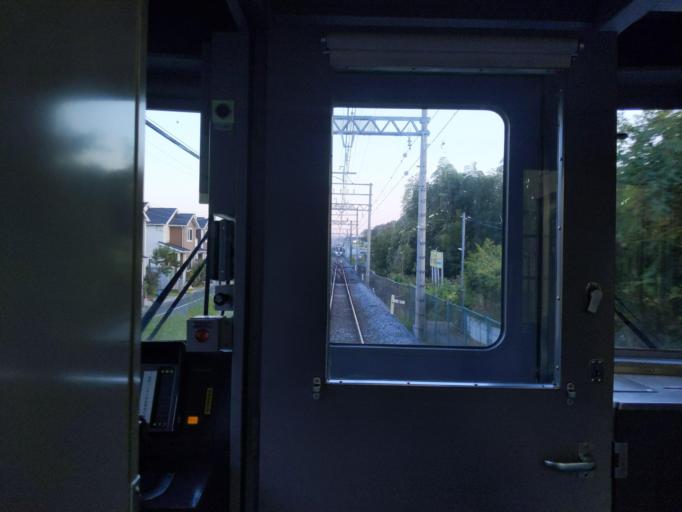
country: JP
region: Chiba
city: Noda
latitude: 35.9610
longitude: 139.8588
